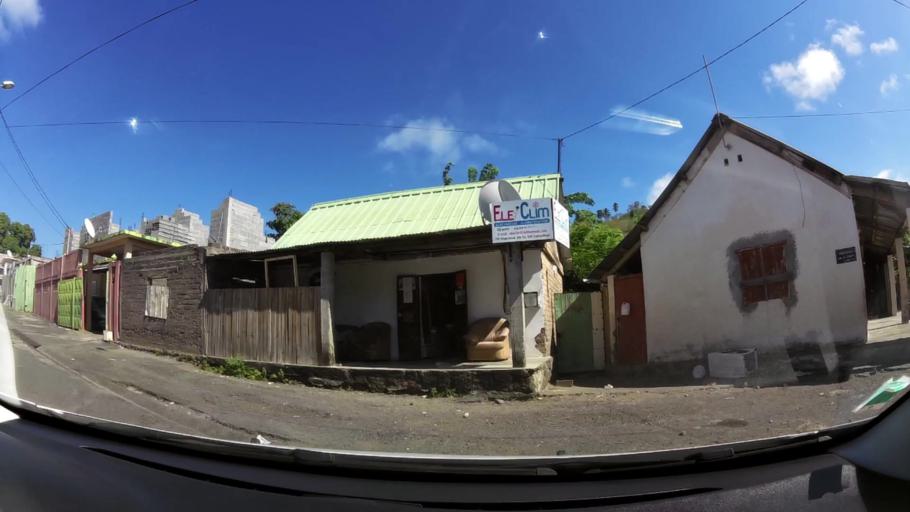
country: YT
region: Pamandzi
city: Pamandzi
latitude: -12.7898
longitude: 45.2791
